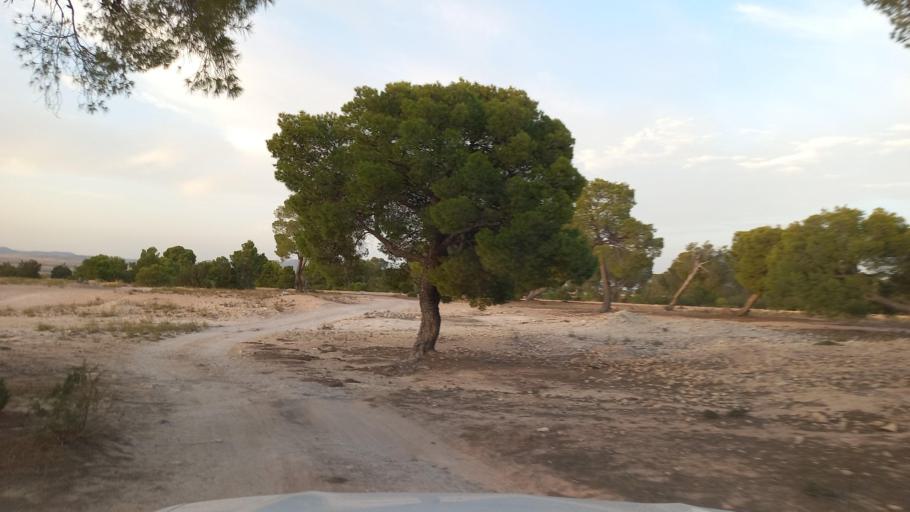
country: TN
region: Al Qasrayn
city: Sbiba
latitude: 35.4262
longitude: 8.9195
